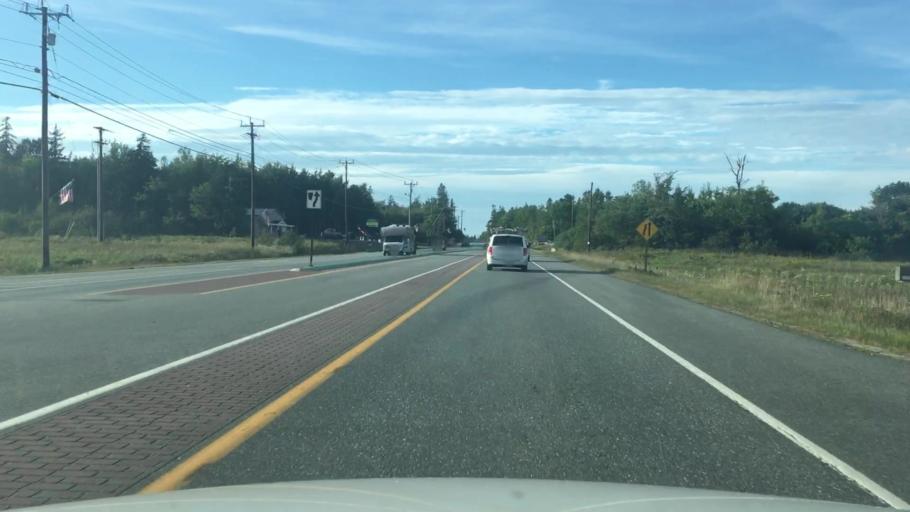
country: US
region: Maine
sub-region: Hancock County
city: Trenton
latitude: 44.4705
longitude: -68.3639
